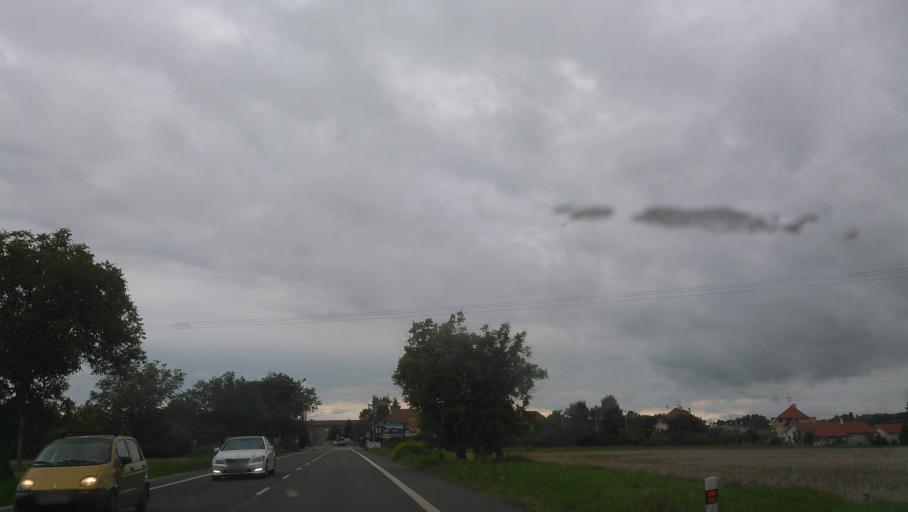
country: SK
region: Trnavsky
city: Dunajska Streda
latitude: 47.9644
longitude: 17.6898
